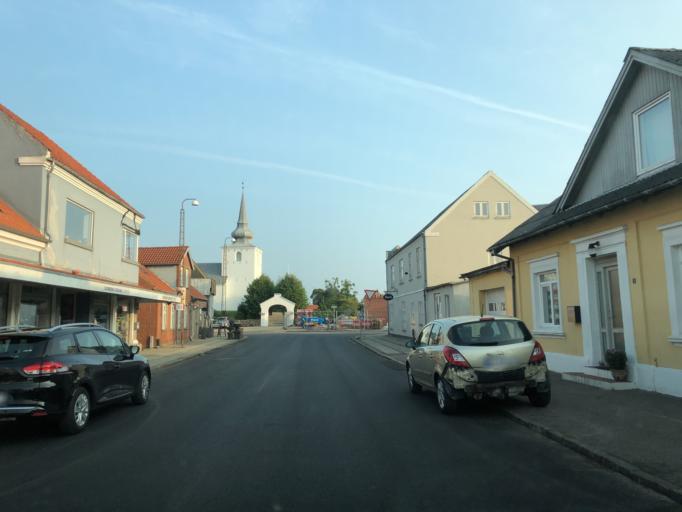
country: DK
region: South Denmark
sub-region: Vejle Kommune
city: Jelling
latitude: 55.7028
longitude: 9.3793
